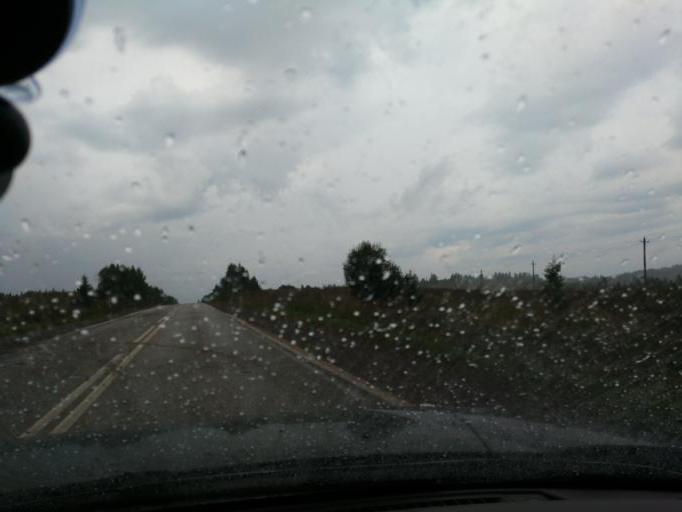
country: RU
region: Perm
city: Barda
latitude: 56.8666
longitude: 55.8979
